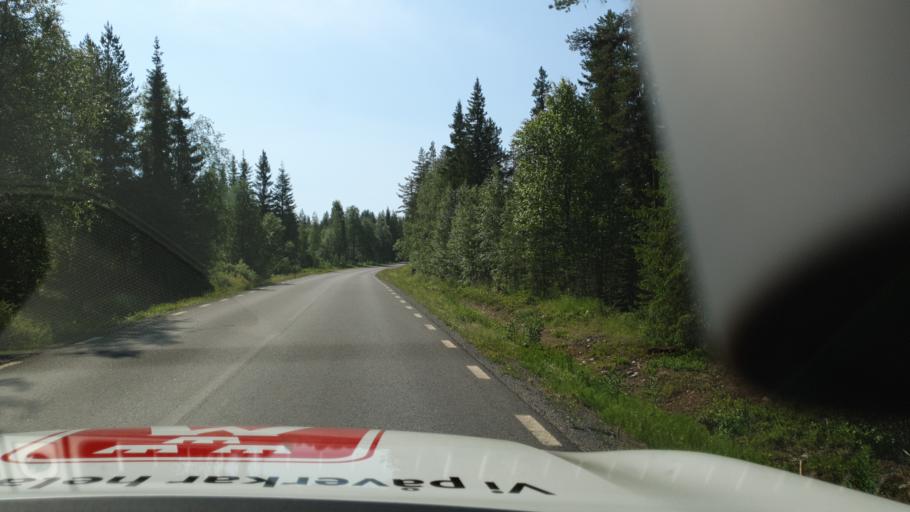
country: SE
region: Vaesterbotten
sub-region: Skelleftea Kommun
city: Langsele
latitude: 64.9951
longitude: 20.0900
